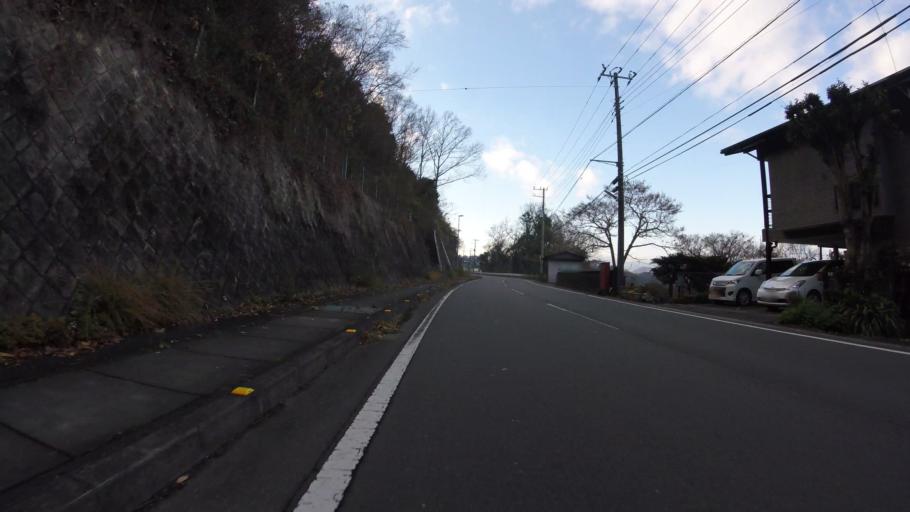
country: JP
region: Shizuoka
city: Mishima
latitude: 35.0999
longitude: 138.9637
